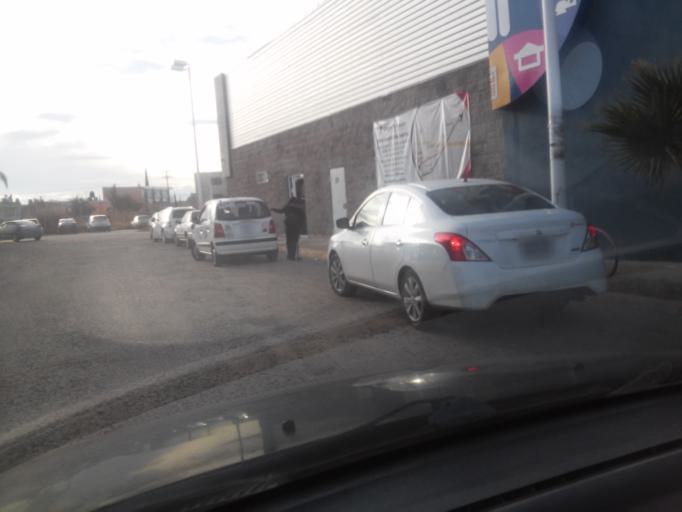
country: MX
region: Durango
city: Victoria de Durango
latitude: 24.0366
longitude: -104.6341
